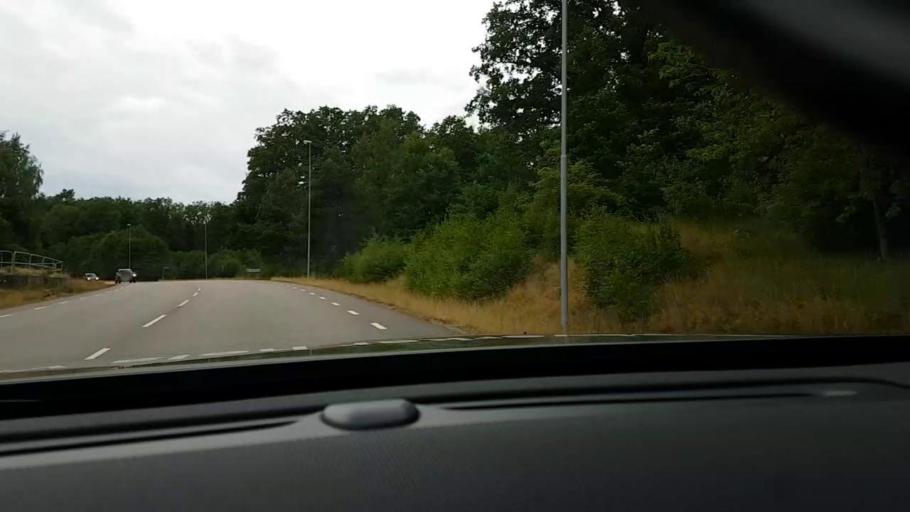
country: SE
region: Skane
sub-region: Hassleholms Kommun
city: Hassleholm
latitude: 56.1683
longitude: 13.7432
